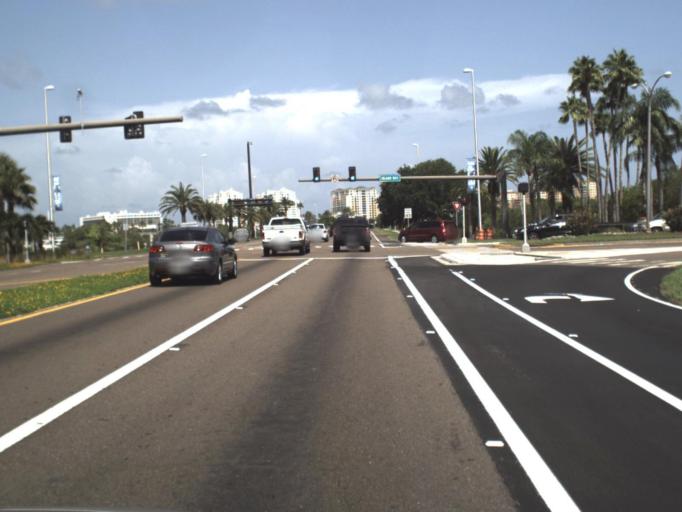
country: US
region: Florida
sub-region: Pinellas County
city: Clearwater
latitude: 27.9745
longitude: -82.8177
